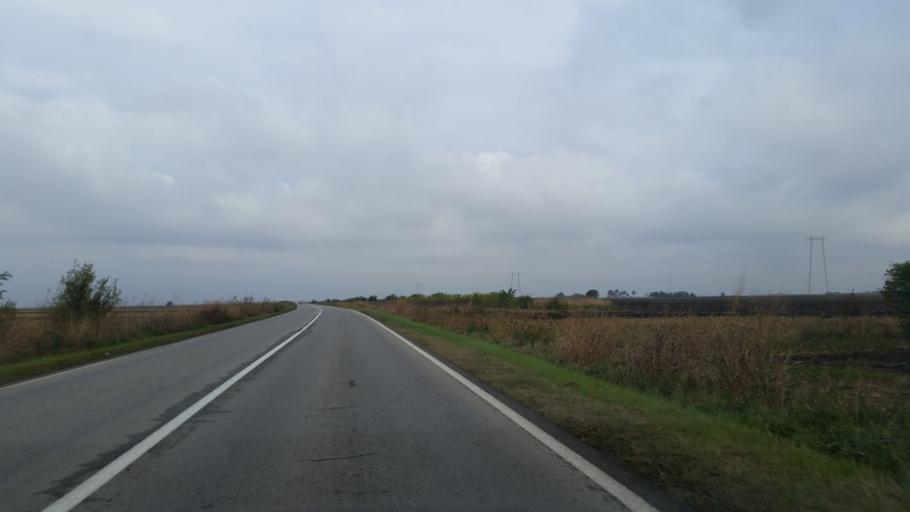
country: RS
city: Elemir
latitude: 45.4513
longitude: 20.3560
